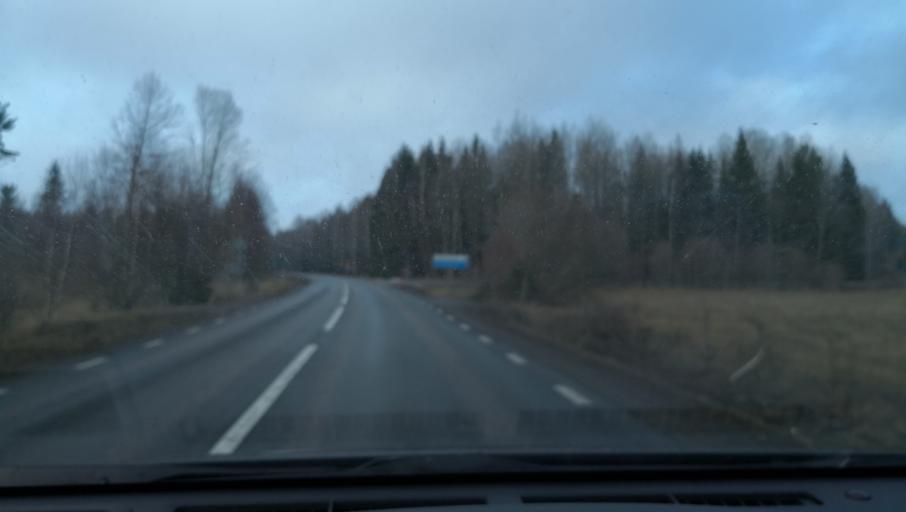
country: SE
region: Vaestra Goetaland
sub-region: Gullspangs Kommun
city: Gullspang
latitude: 58.9541
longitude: 14.0772
